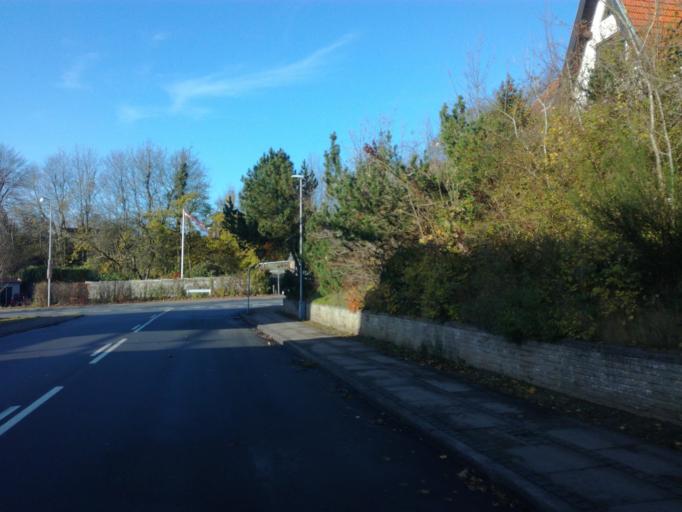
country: DK
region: South Denmark
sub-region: Vejle Kommune
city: Borkop
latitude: 55.6438
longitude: 9.6548
